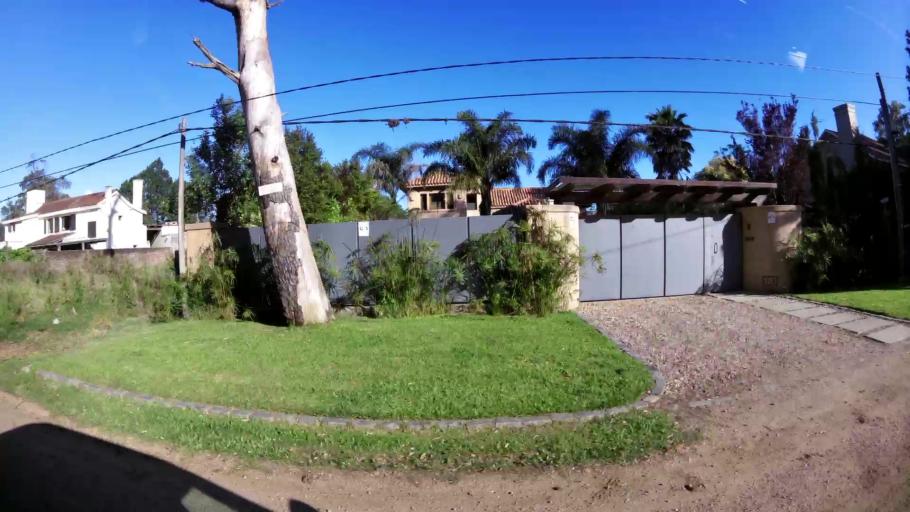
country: UY
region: Canelones
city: Paso de Carrasco
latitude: -34.8579
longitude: -56.0378
